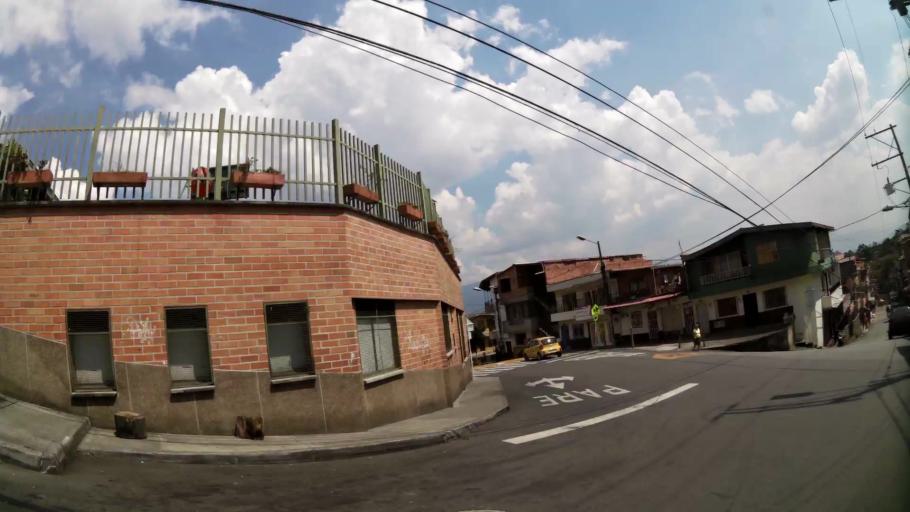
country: CO
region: Antioquia
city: Medellin
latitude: 6.2874
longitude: -75.5825
